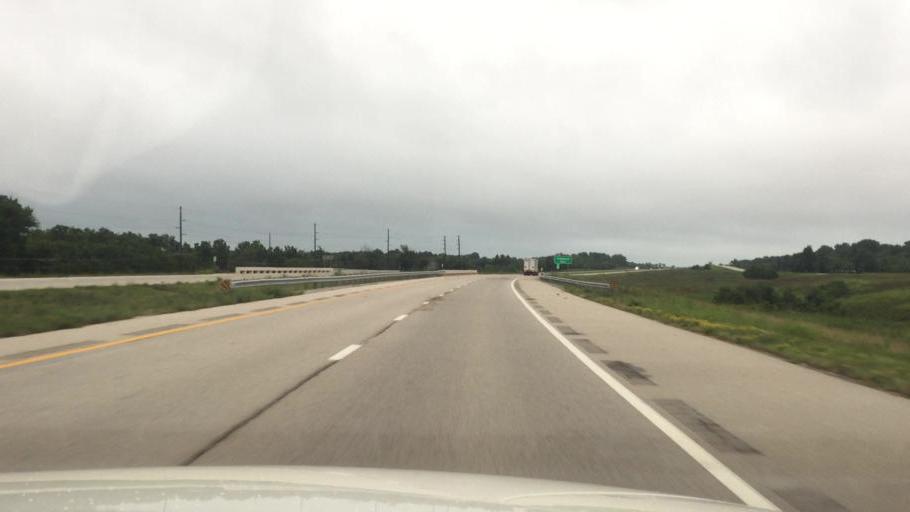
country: US
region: Kansas
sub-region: Montgomery County
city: Coffeyville
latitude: 37.0682
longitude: -95.5846
